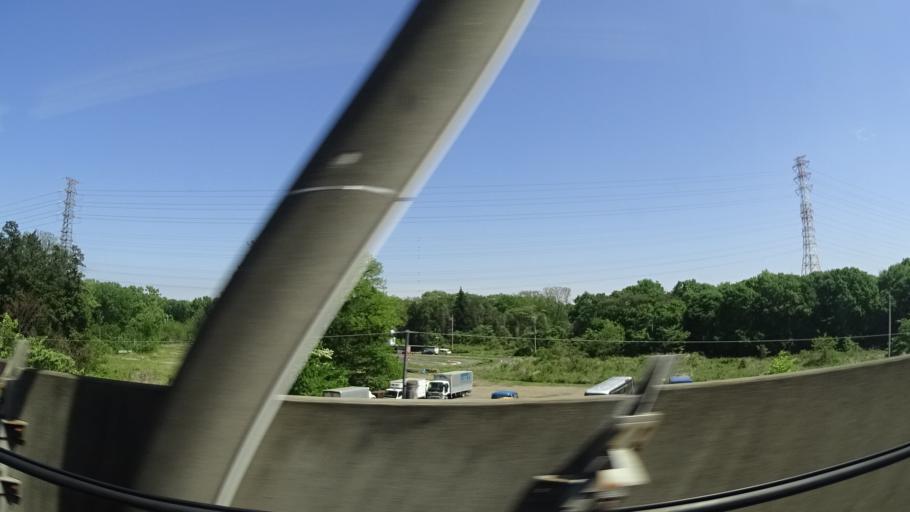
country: JP
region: Tochigi
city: Oyama
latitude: 36.3431
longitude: 139.8238
